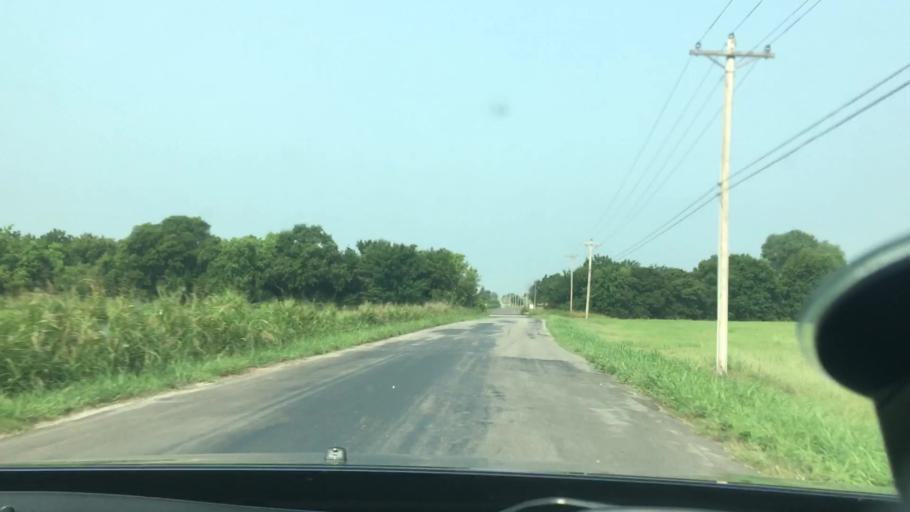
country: US
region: Oklahoma
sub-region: Garvin County
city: Lindsay
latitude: 34.8120
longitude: -97.6231
